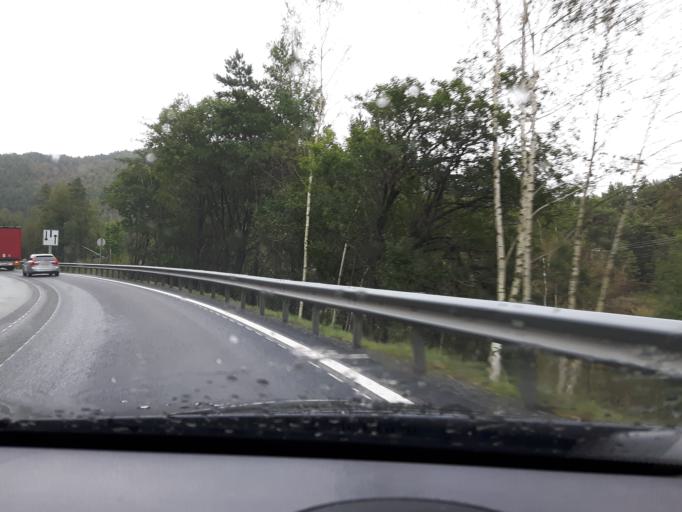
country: NO
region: Vest-Agder
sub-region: Sogne
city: Sogne
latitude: 58.1002
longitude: 7.6529
